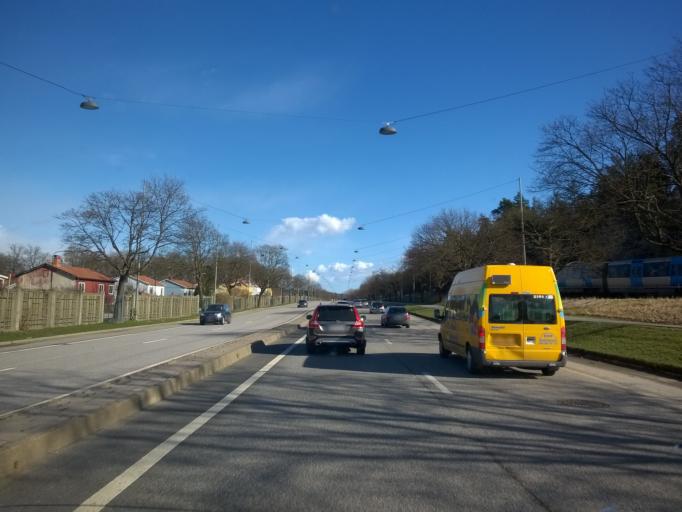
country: SE
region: Stockholm
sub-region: Stockholms Kommun
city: Bromma
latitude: 59.3457
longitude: 17.8970
